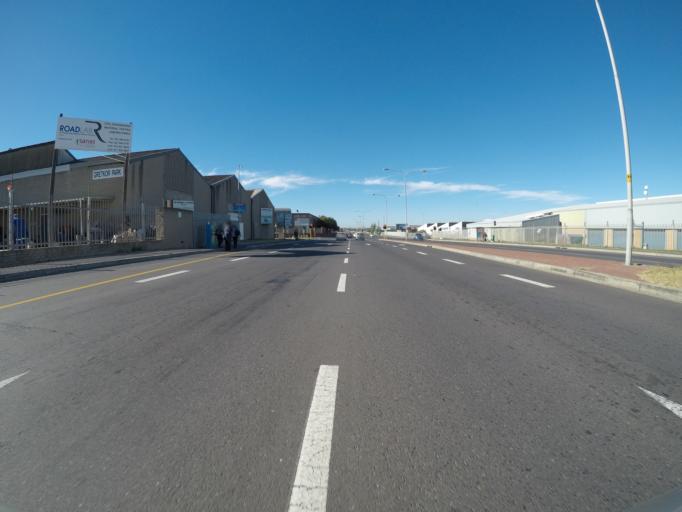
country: ZA
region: Western Cape
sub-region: City of Cape Town
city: Kraaifontein
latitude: -33.9002
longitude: 18.6700
